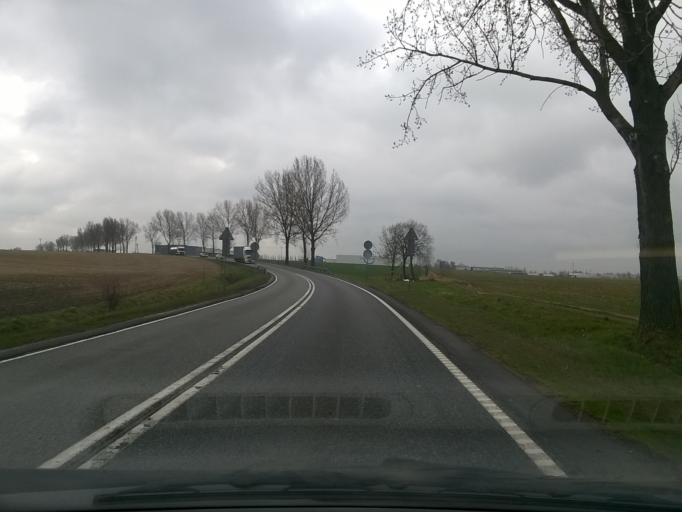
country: PL
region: Kujawsko-Pomorskie
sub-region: Powiat zninski
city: Znin
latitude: 52.8694
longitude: 17.7006
